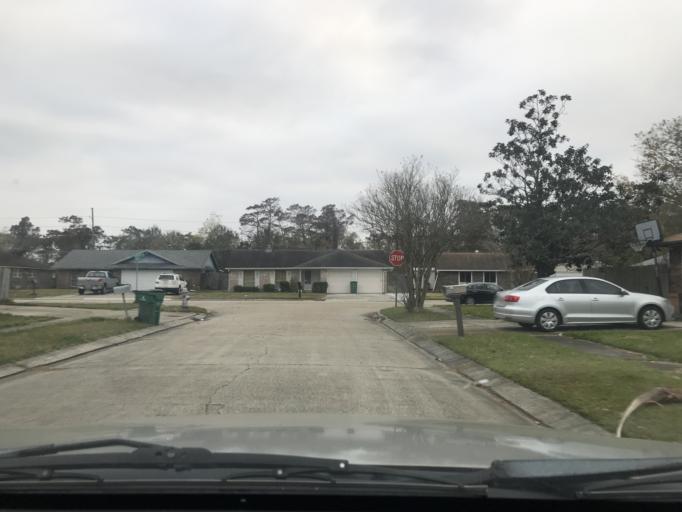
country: US
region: Louisiana
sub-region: Jefferson Parish
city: Woodmere
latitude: 29.8617
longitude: -90.0859
